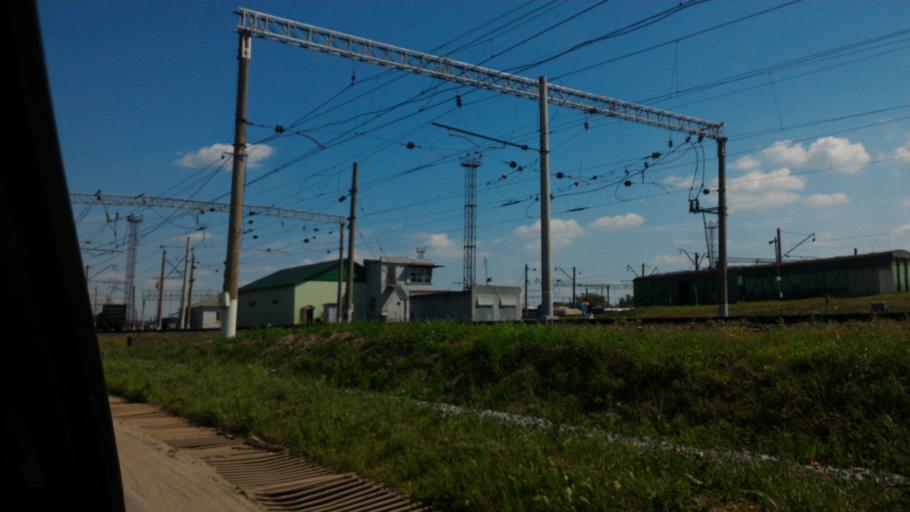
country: RU
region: Rjazan
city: Rybnoye
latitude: 54.7300
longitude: 39.5073
